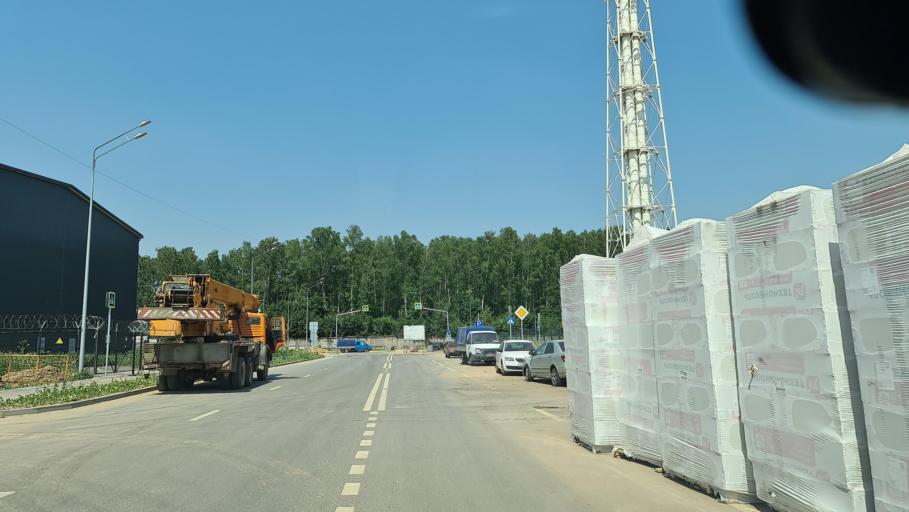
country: RU
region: Moscow
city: Ivanovskoye
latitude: 55.7867
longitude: 37.8458
